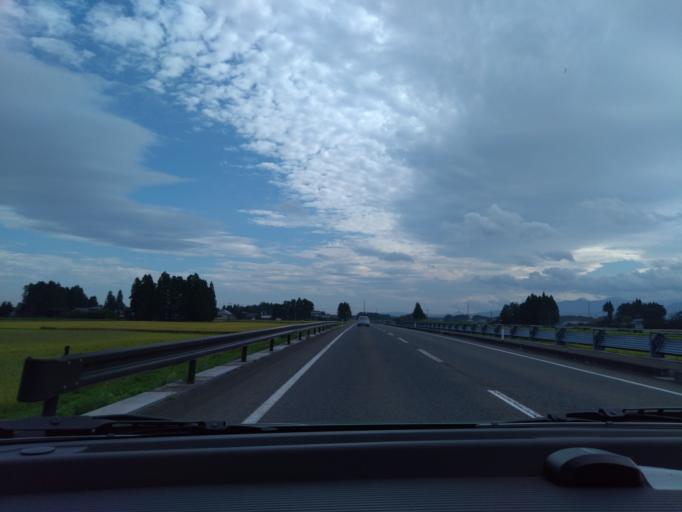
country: JP
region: Iwate
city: Hanamaki
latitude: 39.3521
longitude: 141.0536
